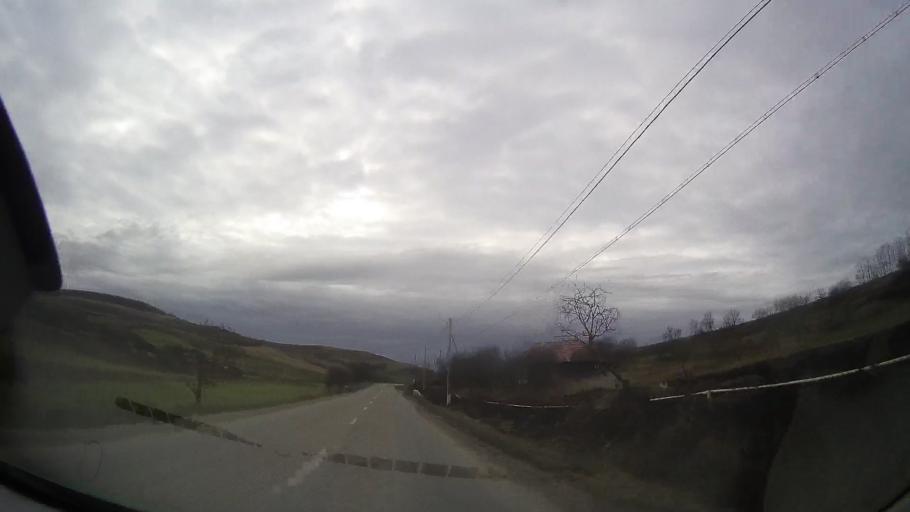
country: RO
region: Bistrita-Nasaud
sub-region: Comuna Budesti
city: Budesti
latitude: 46.8537
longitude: 24.2431
